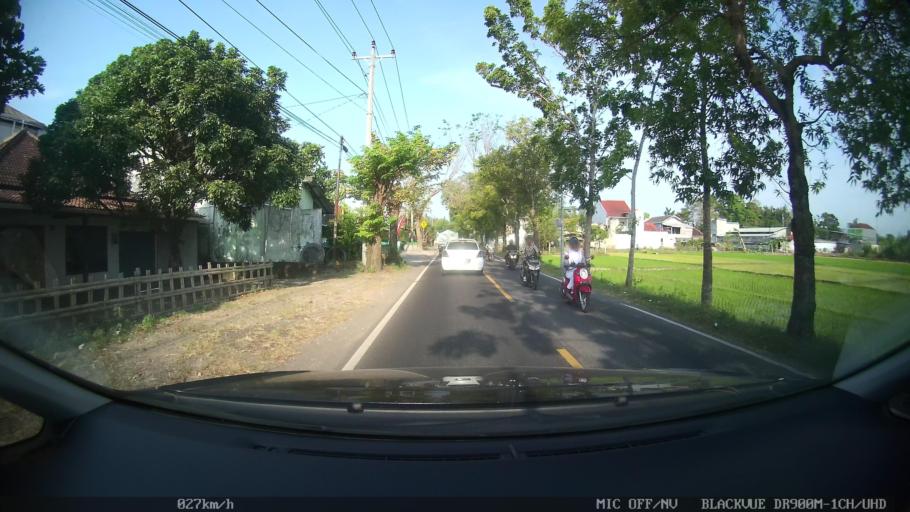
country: ID
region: Daerah Istimewa Yogyakarta
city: Bantul
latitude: -7.8787
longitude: 110.3301
